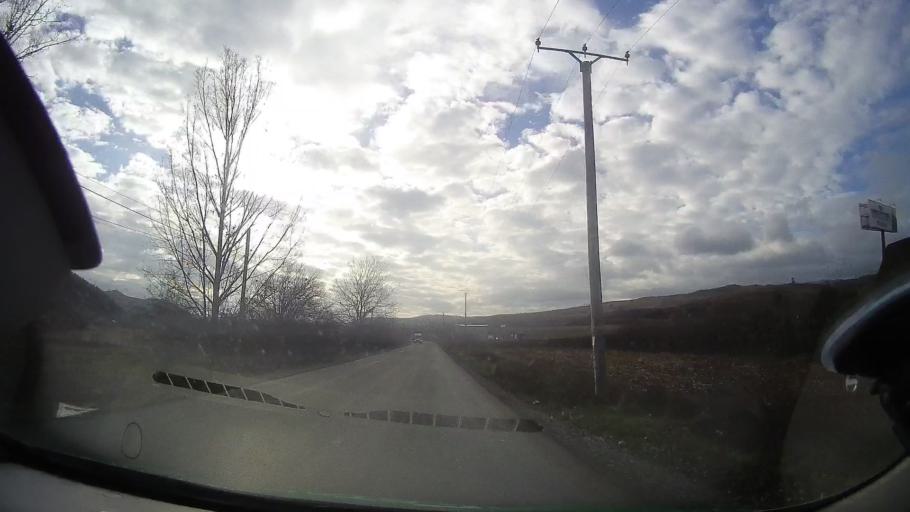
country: RO
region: Cluj
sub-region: Comuna Floresti
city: Luna de Sus
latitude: 46.7256
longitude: 23.4197
